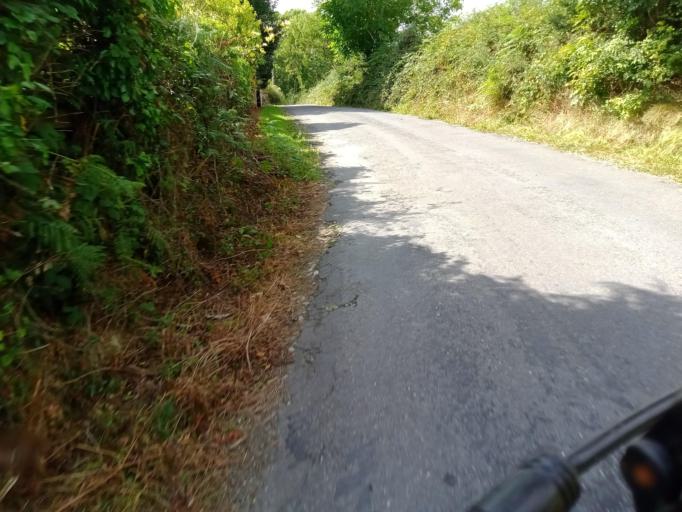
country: IE
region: Munster
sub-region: Waterford
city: Dungarvan
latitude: 52.1363
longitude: -7.4726
